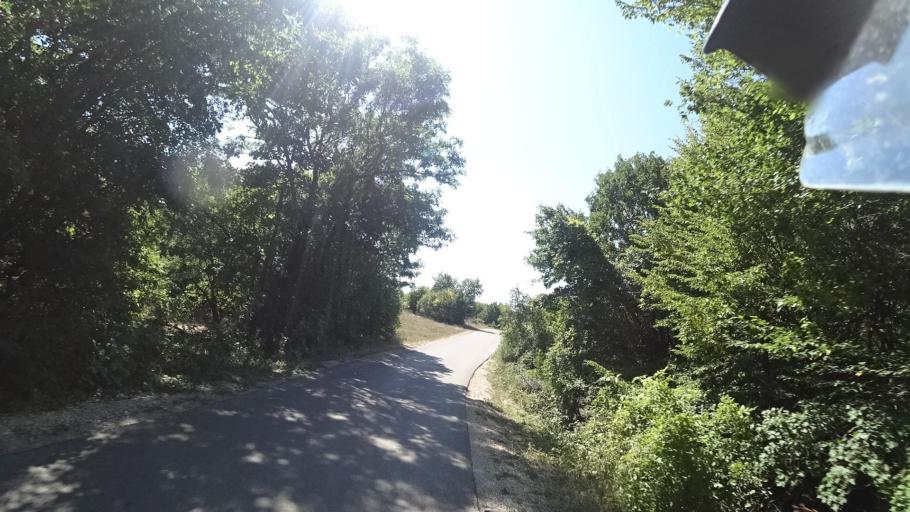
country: HR
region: Licko-Senjska
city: Otocac
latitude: 44.7345
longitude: 15.3532
